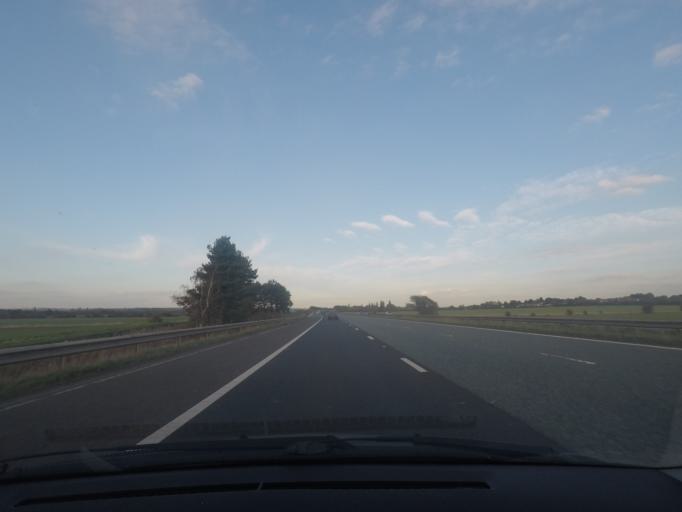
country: GB
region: England
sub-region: North Lincolnshire
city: Brigg
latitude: 53.5663
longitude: -0.4806
